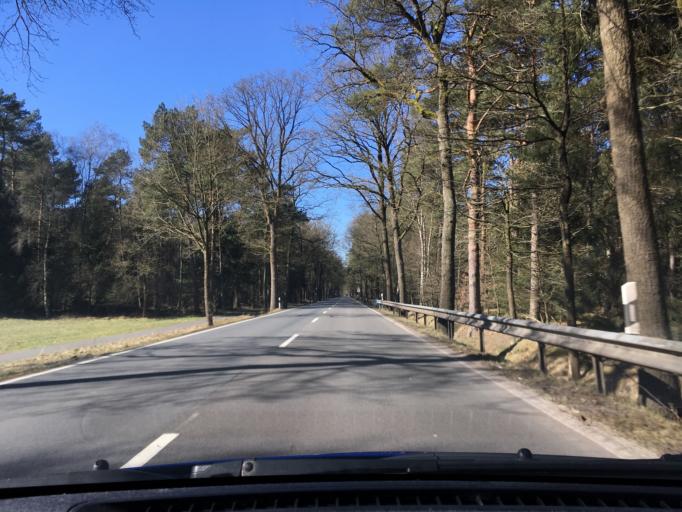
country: DE
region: Lower Saxony
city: Brockel
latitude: 53.0905
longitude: 9.5579
